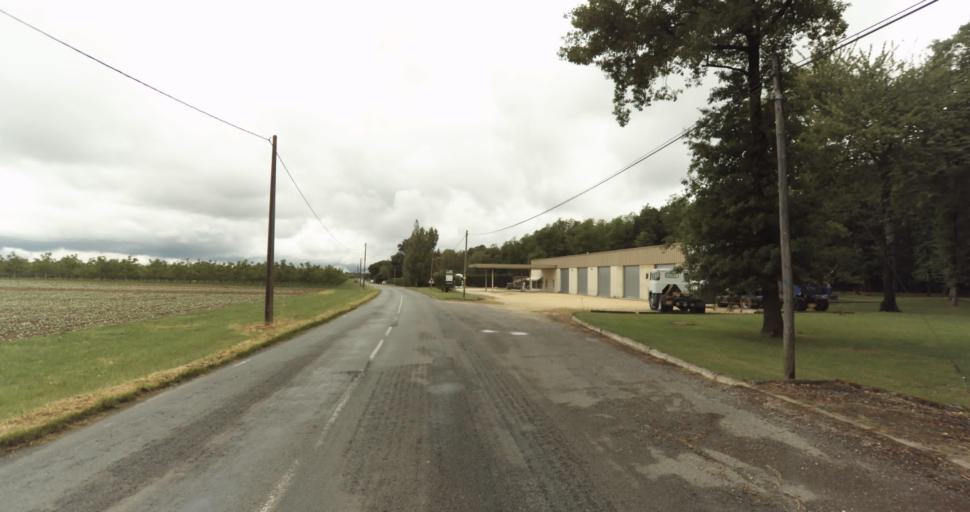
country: FR
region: Aquitaine
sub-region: Departement de la Dordogne
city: Beaumont-du-Perigord
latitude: 44.7313
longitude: 0.7885
